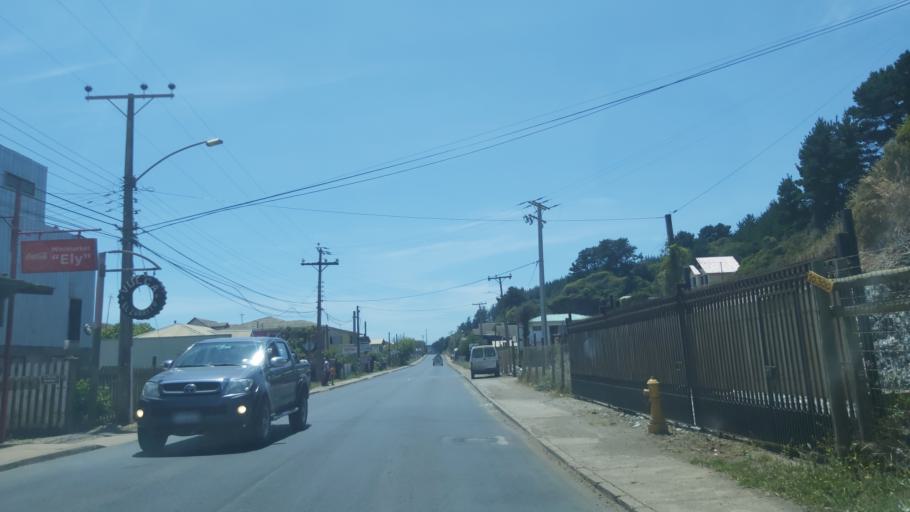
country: CL
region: Maule
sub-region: Provincia de Cauquenes
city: Cauquenes
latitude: -35.8414
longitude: -72.6294
